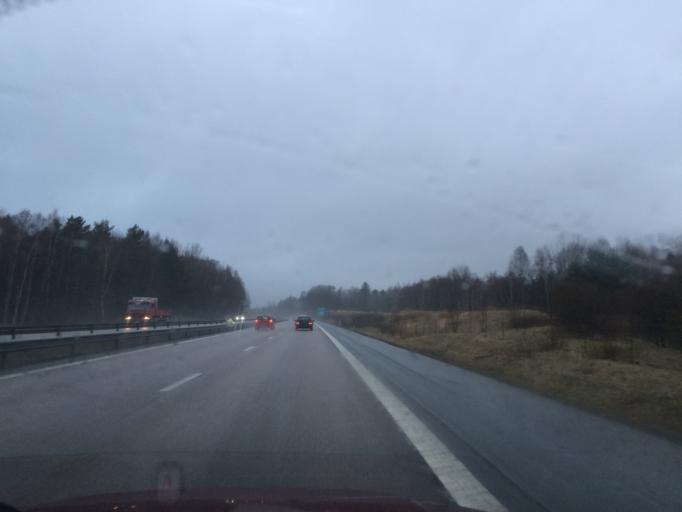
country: SE
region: Vaestra Goetaland
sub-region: Molndal
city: Lindome
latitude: 57.5828
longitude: 12.0631
